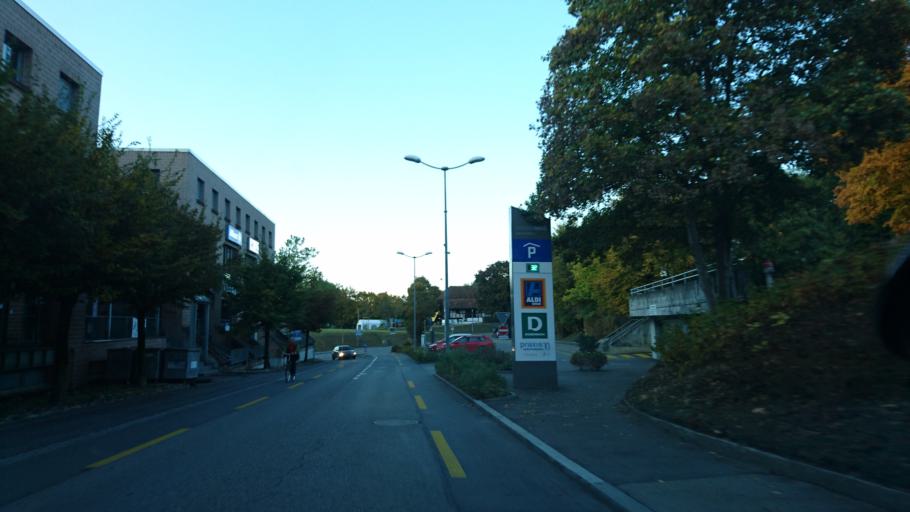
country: CH
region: Bern
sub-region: Bern-Mittelland District
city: Munsingen
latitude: 46.8742
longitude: 7.5596
